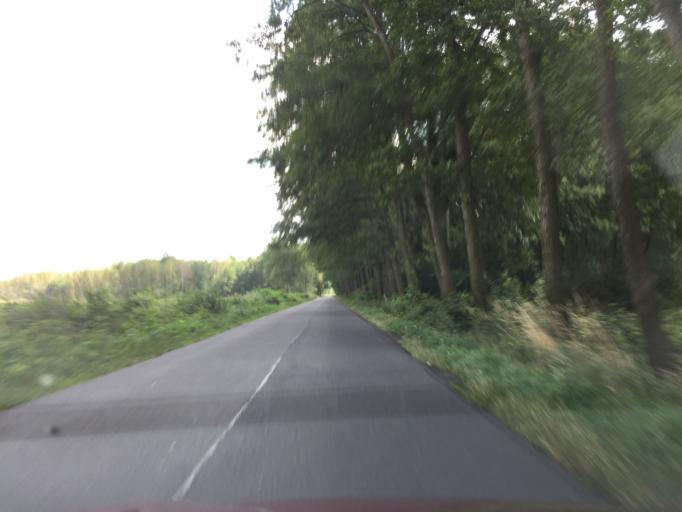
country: PL
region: Greater Poland Voivodeship
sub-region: Powiat kaliski
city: Stawiszyn
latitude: 51.9483
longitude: 18.1712
